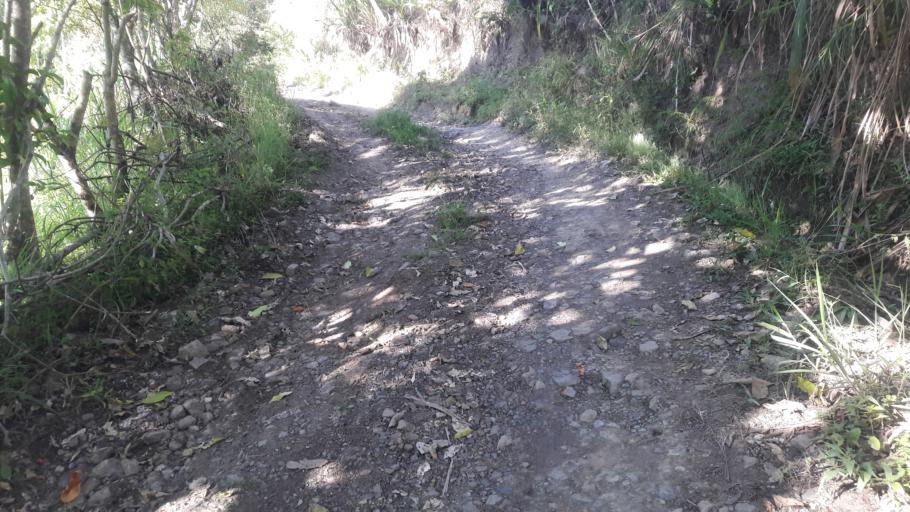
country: CO
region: Cundinamarca
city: Tenza
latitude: 5.0875
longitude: -73.4180
